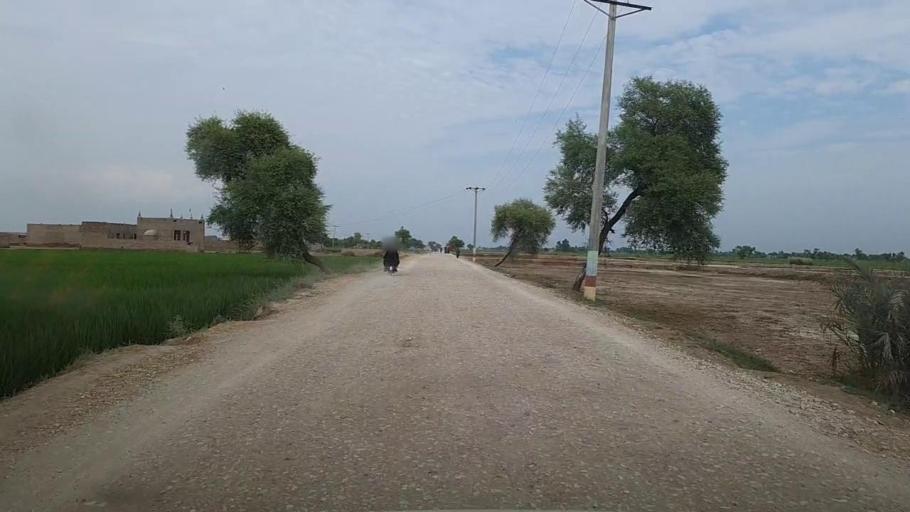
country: PK
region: Sindh
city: Thul
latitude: 28.2460
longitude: 68.7878
